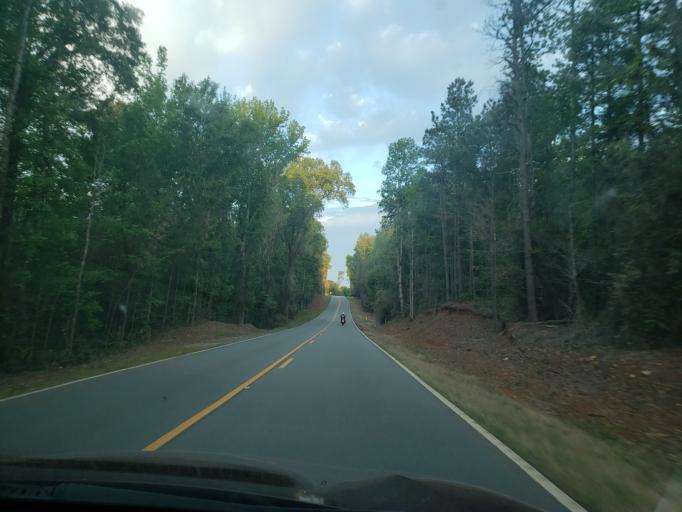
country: US
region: Alabama
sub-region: Tallapoosa County
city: Dadeville
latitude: 32.7105
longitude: -85.7784
